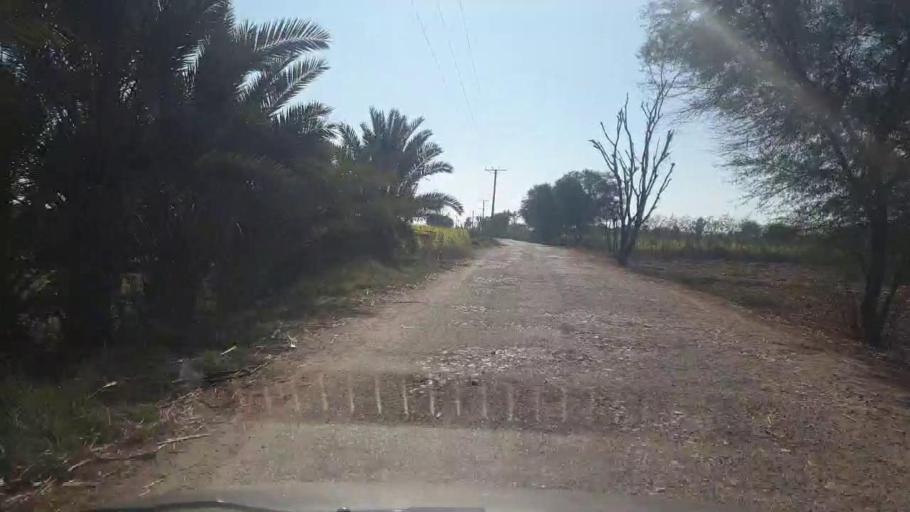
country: PK
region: Sindh
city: Bozdar
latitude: 27.2663
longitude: 68.6521
